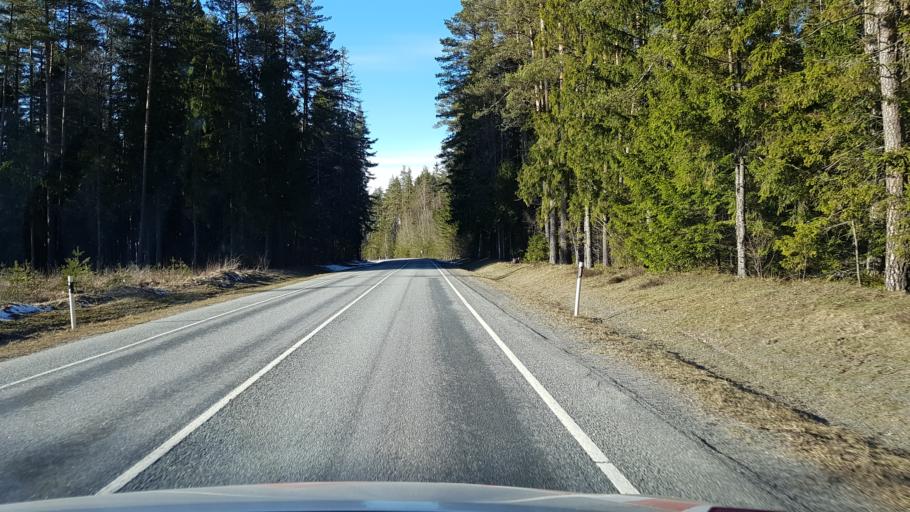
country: EE
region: Laeaene-Virumaa
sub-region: Tapa vald
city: Tapa
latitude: 59.4214
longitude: 25.9908
